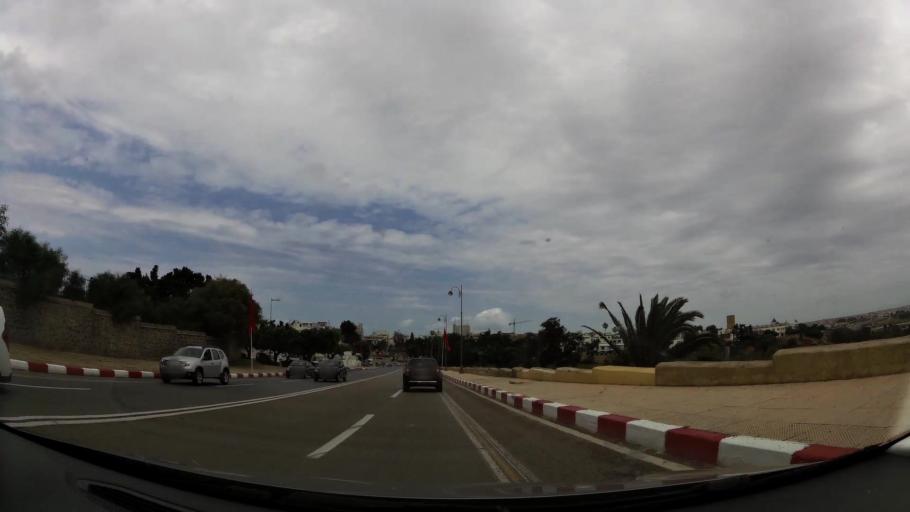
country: MA
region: Rabat-Sale-Zemmour-Zaer
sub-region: Rabat
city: Rabat
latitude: 34.0154
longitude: -6.8198
